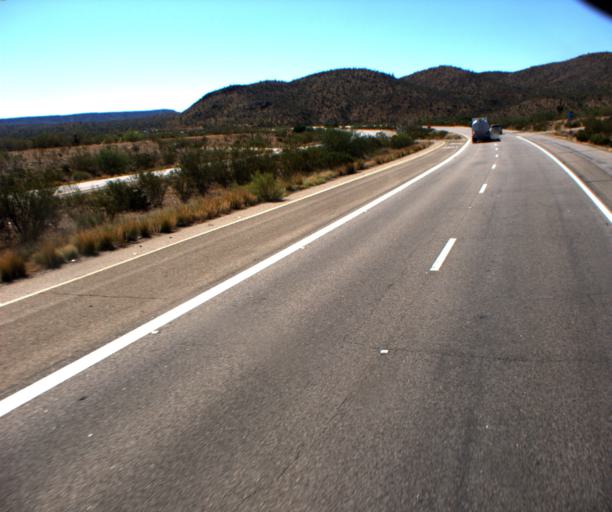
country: US
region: Arizona
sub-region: Yavapai County
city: Bagdad
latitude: 34.3729
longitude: -113.1894
